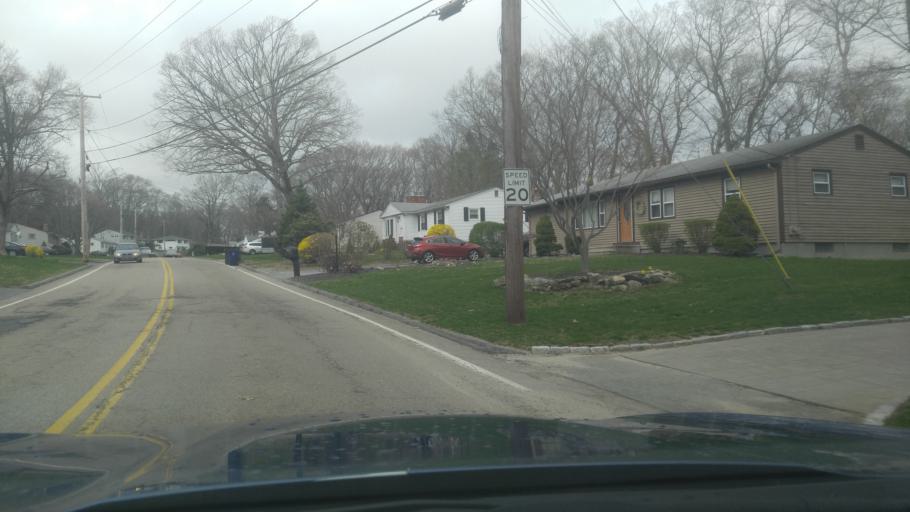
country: US
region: Rhode Island
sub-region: Kent County
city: East Greenwich
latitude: 41.6870
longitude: -71.4719
